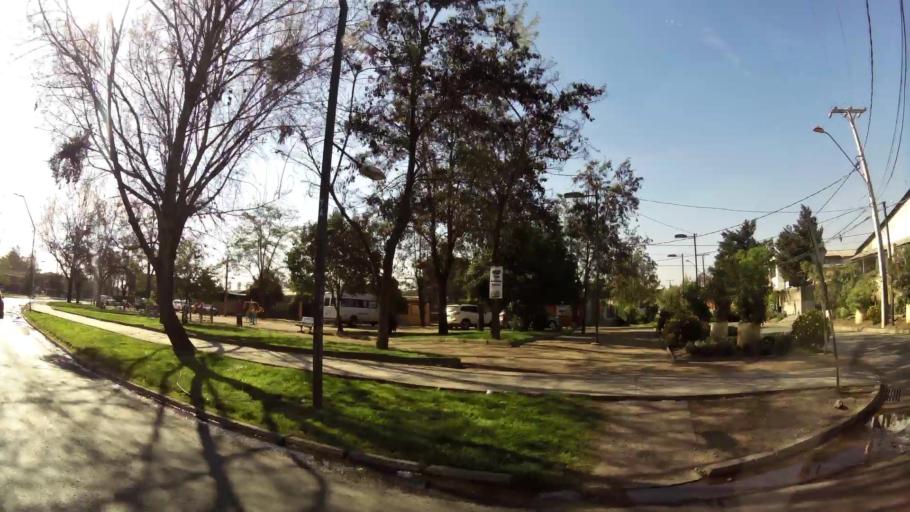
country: CL
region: Santiago Metropolitan
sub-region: Provincia de Santiago
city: Villa Presidente Frei, Nunoa, Santiago, Chile
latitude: -33.4665
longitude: -70.5627
